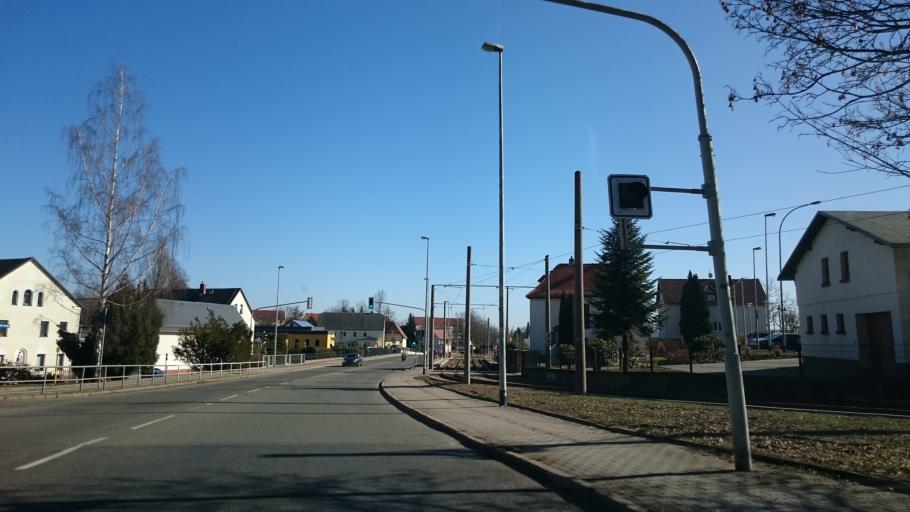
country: DE
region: Saxony
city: Lichtentanne
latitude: 50.7226
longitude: 12.4450
